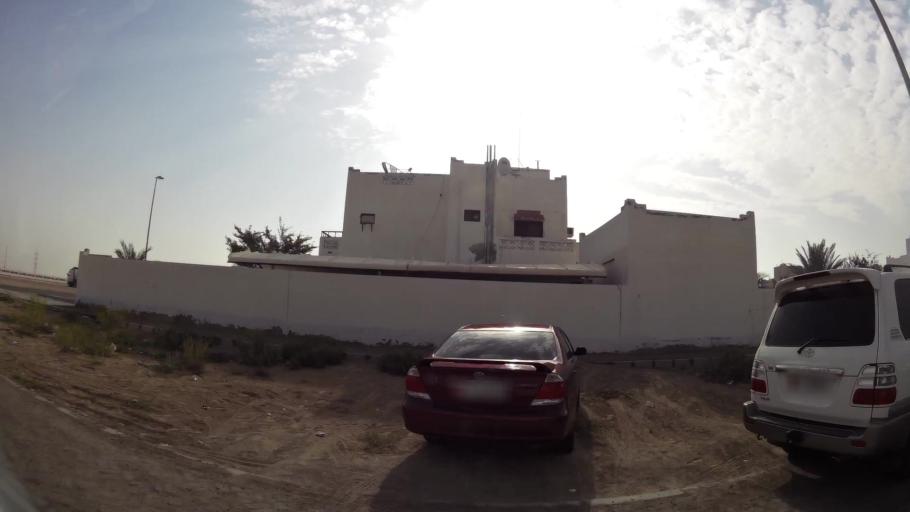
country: AE
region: Abu Dhabi
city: Abu Dhabi
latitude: 24.2415
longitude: 54.7191
